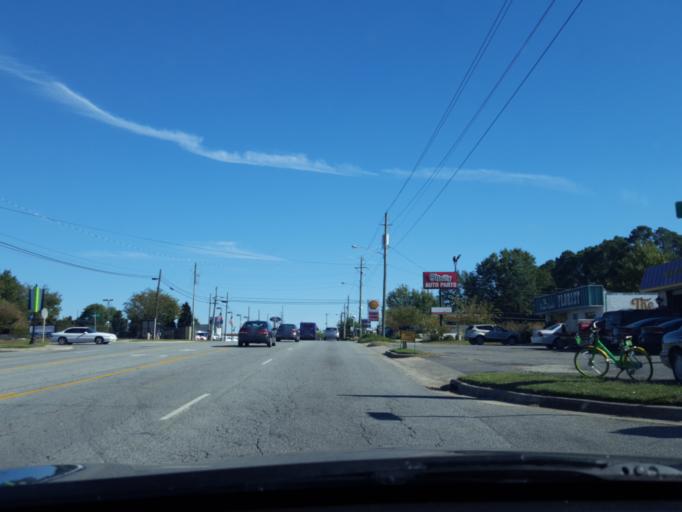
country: US
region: North Carolina
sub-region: Pitt County
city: Greenville
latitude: 35.6022
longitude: -77.3387
